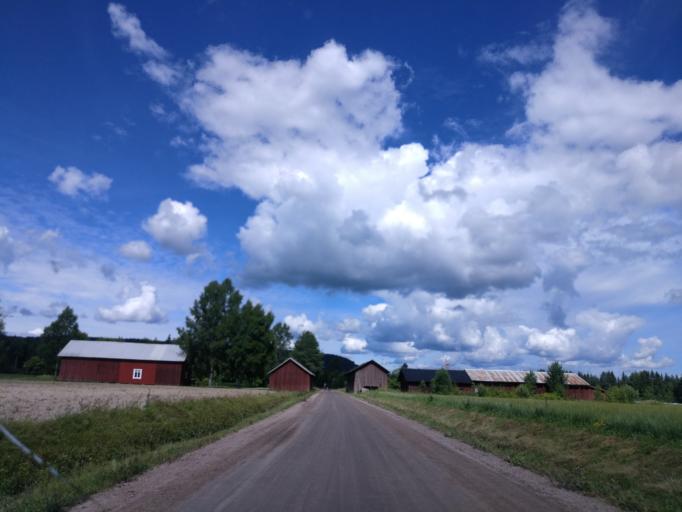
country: SE
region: Vaermland
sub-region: Hagfors Kommun
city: Ekshaerad
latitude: 60.0461
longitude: 13.4924
